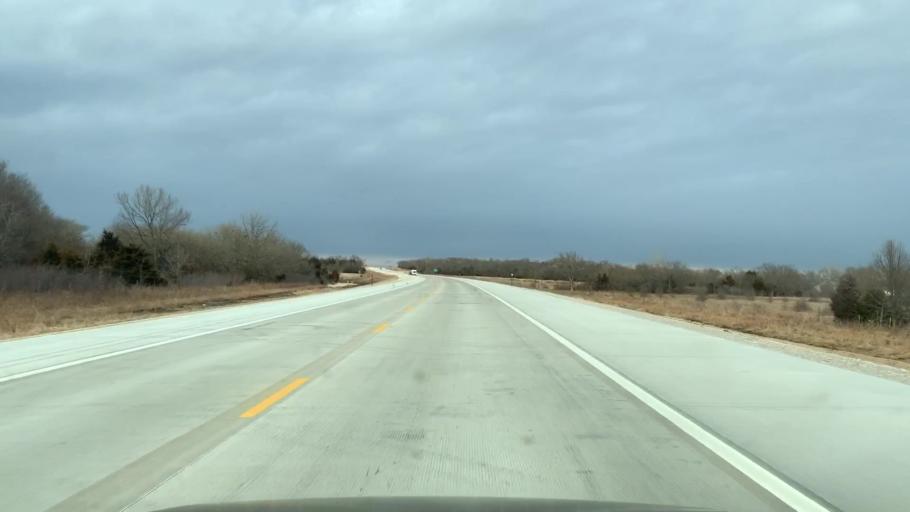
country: US
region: Kansas
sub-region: Allen County
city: Humboldt
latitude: 37.8620
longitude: -95.4044
